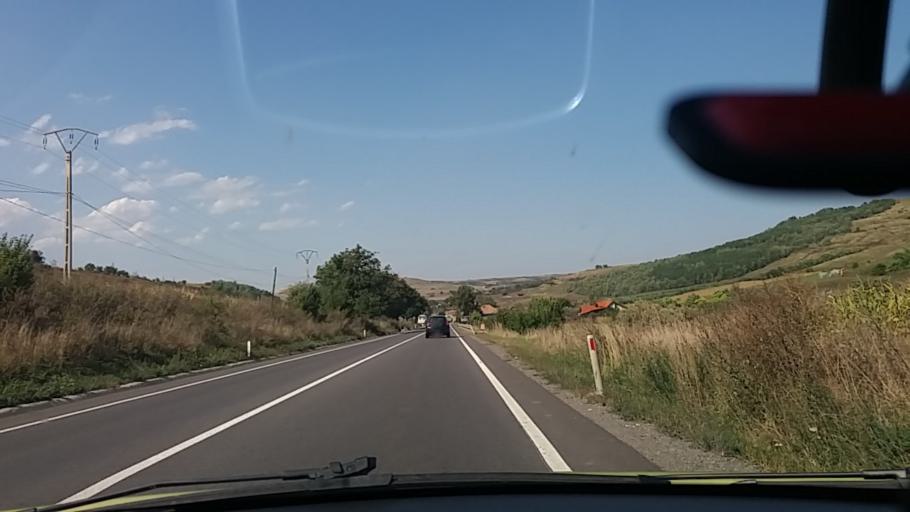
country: RO
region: Sibiu
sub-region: Comuna Slimnic
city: Slimnic
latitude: 45.9020
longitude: 24.1602
